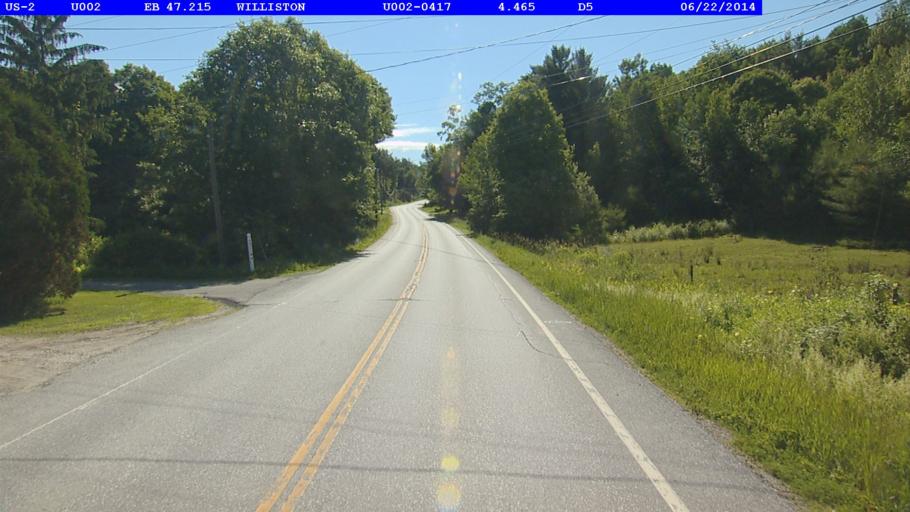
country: US
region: Vermont
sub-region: Chittenden County
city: Williston
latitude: 44.4348
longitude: -73.0541
